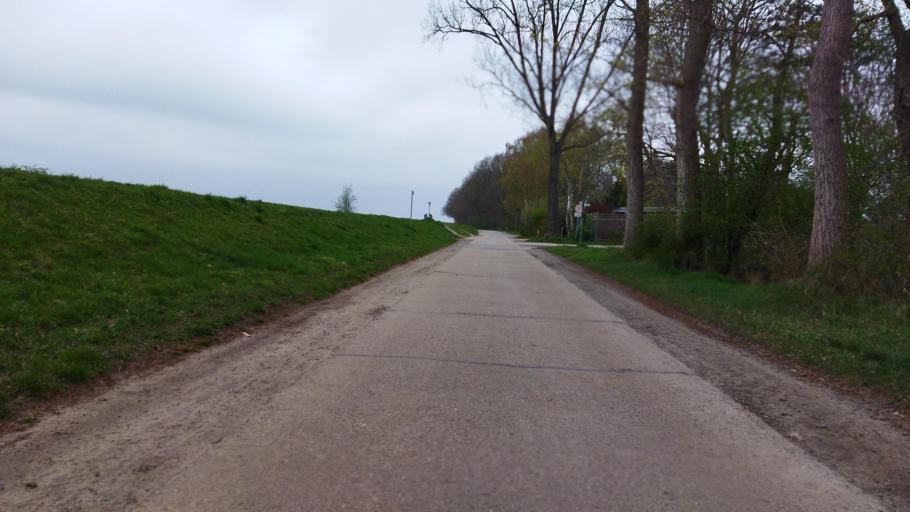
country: DE
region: Lower Saxony
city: Achim
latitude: 53.0112
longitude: 9.0013
